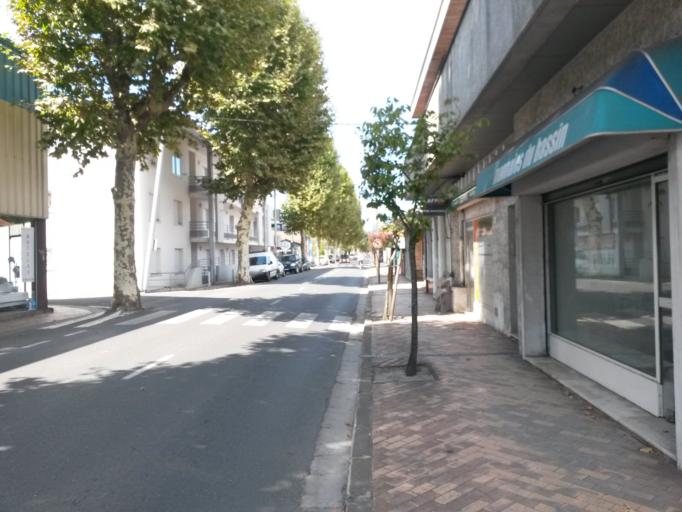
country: FR
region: Aquitaine
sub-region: Departement de la Gironde
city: Andernos-les-Bains
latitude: 44.7383
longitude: -1.0913
